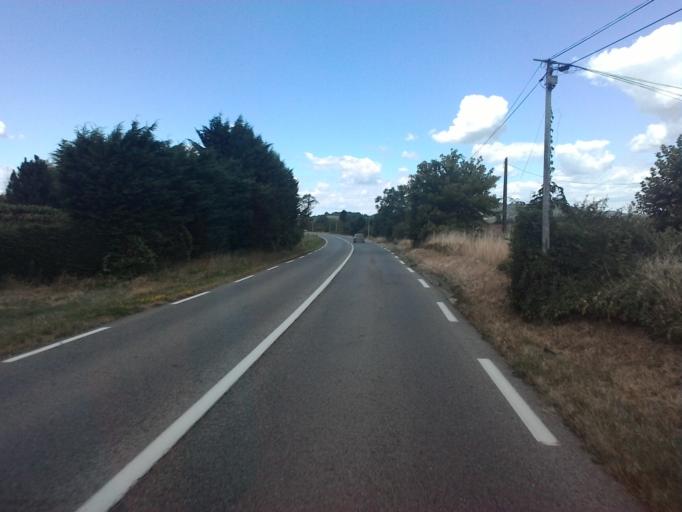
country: FR
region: Rhone-Alpes
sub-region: Departement de l'Ain
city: Saint-Sorlin-en-Bugey
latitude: 45.8740
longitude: 5.3613
